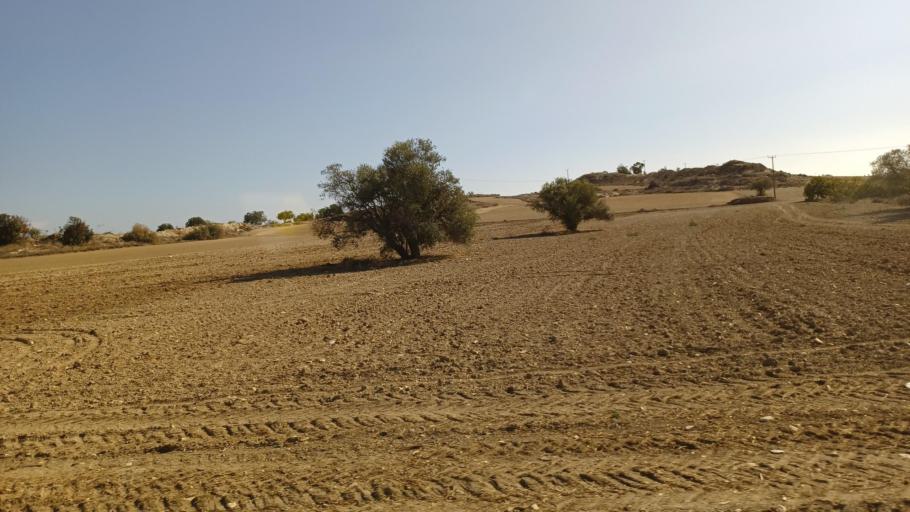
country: CY
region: Larnaka
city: Voroklini
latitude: 34.9912
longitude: 33.6669
